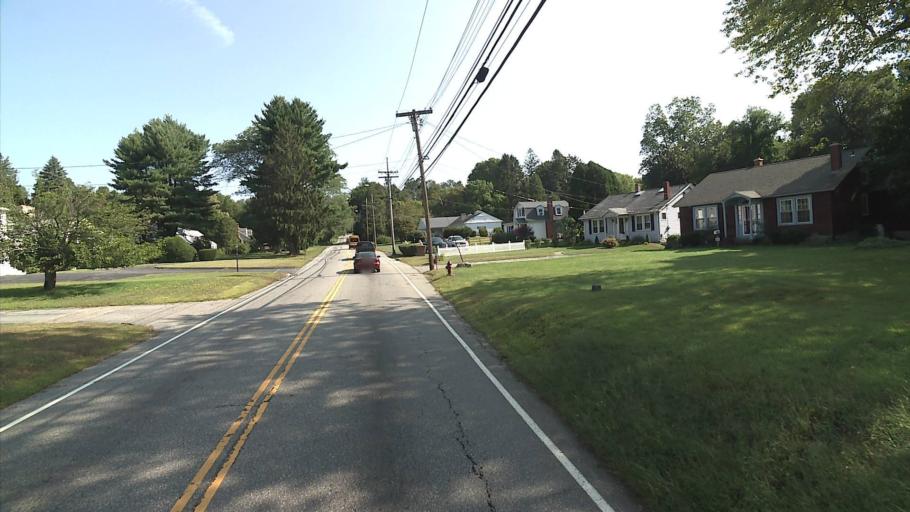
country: US
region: Connecticut
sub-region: New London County
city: Norwich
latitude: 41.5514
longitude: -72.0822
